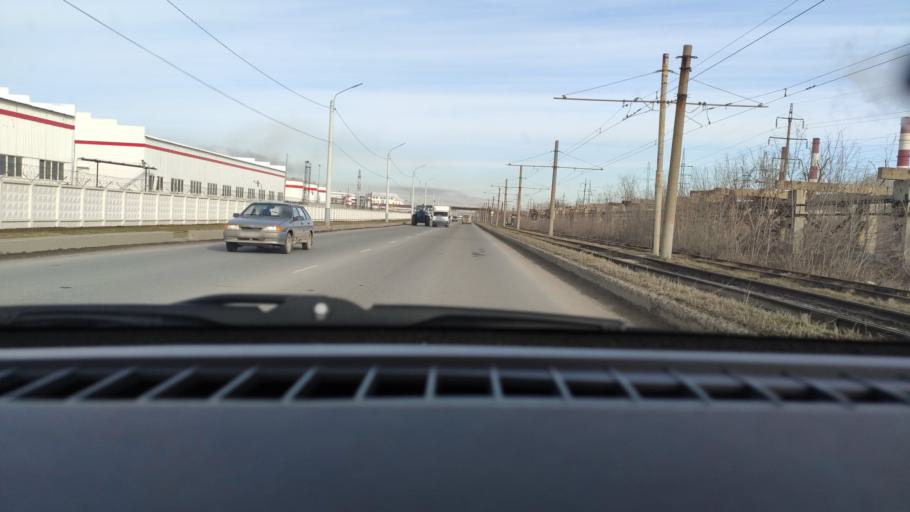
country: RU
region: Perm
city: Gamovo
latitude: 57.9177
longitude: 56.1505
